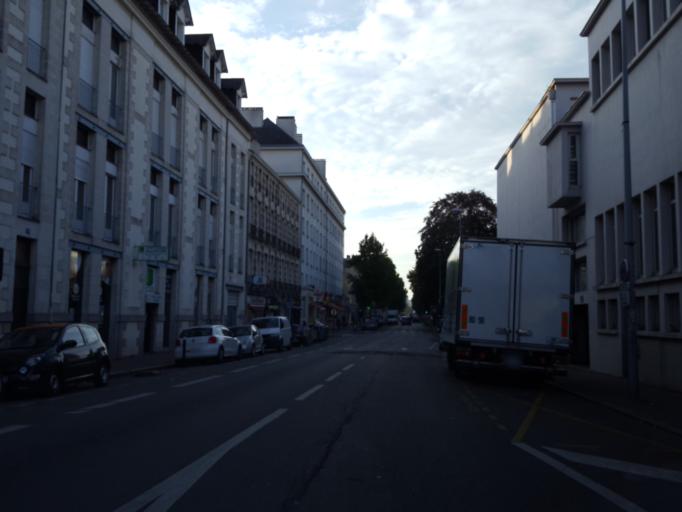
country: FR
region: Pays de la Loire
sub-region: Departement de la Loire-Atlantique
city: Nantes
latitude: 47.2122
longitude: -1.5526
